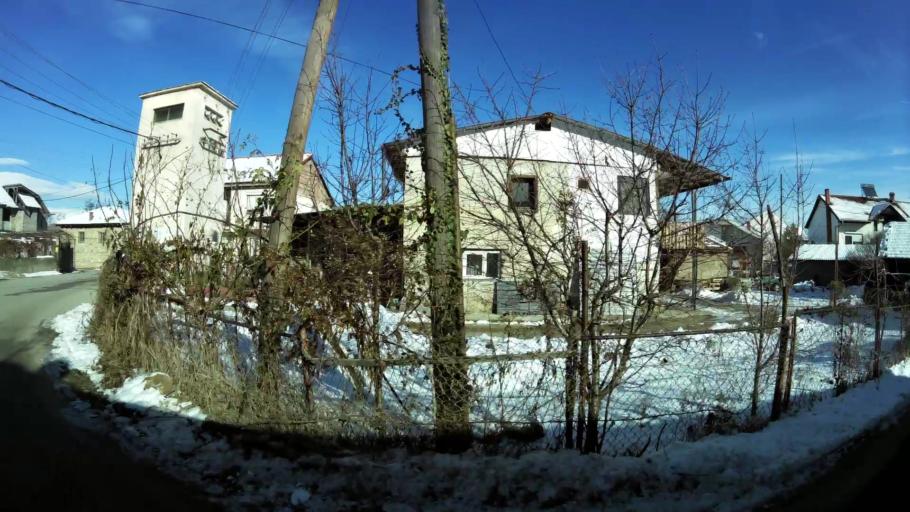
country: MK
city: Grchec
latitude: 41.9751
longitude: 21.3102
